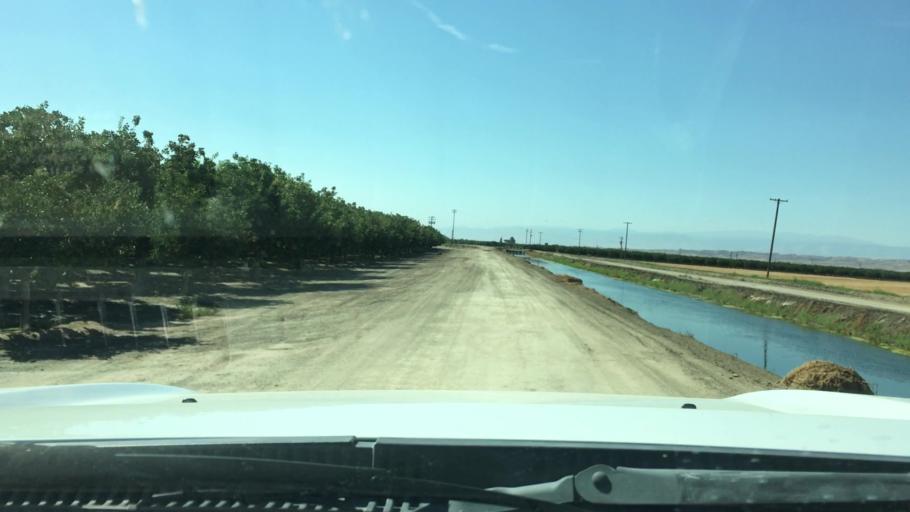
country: US
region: California
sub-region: Kern County
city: Buttonwillow
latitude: 35.3679
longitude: -119.3976
